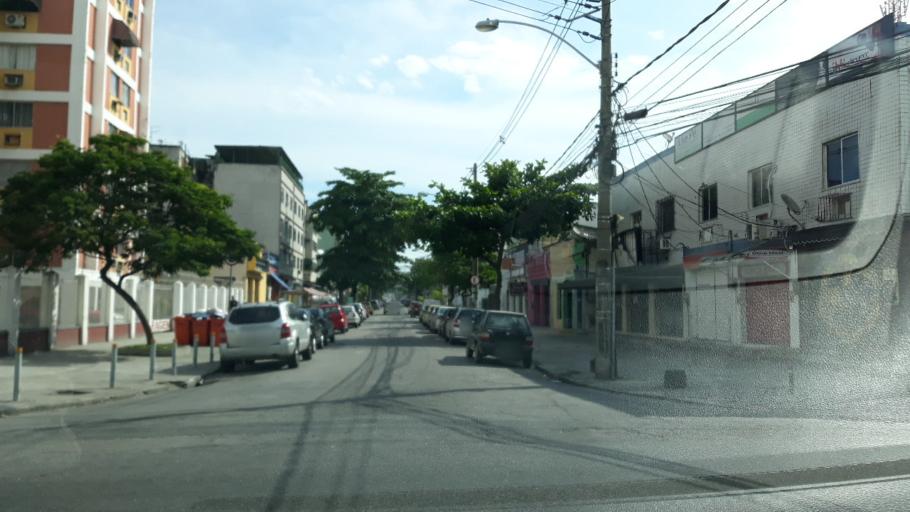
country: BR
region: Rio de Janeiro
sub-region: Duque De Caxias
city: Duque de Caxias
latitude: -22.8375
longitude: -43.2767
